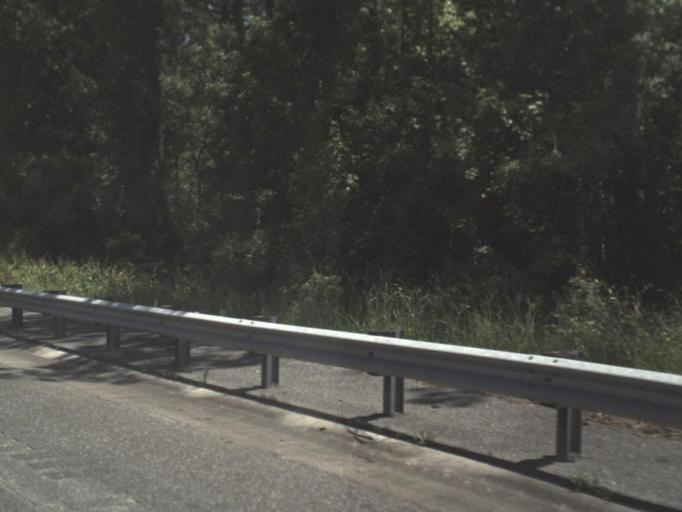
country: US
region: Florida
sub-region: Jefferson County
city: Monticello
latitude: 30.4730
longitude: -83.8592
